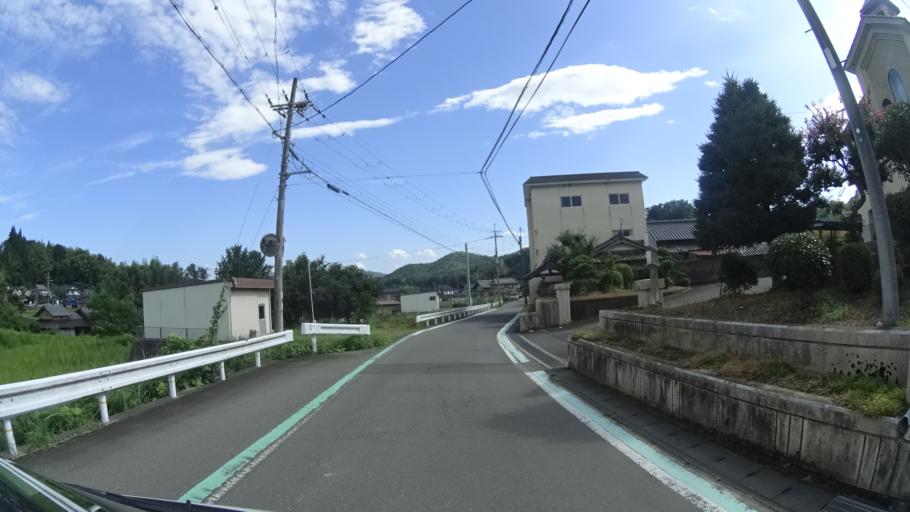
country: JP
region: Kyoto
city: Fukuchiyama
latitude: 35.3270
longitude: 135.1770
